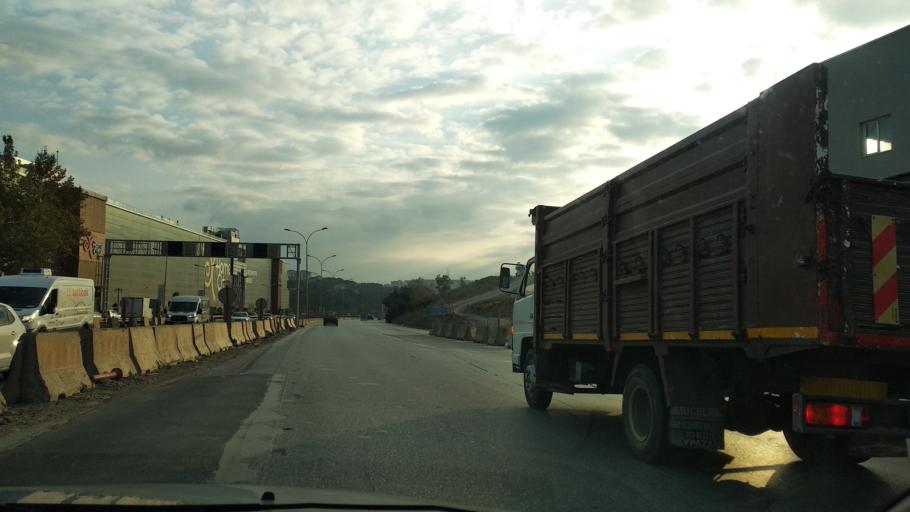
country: TR
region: Istanbul
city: Icmeler
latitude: 40.8892
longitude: 29.3251
